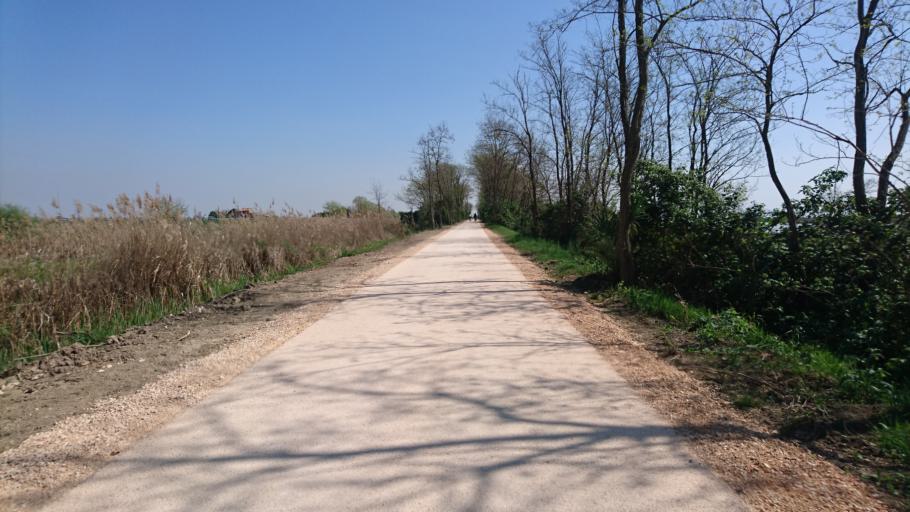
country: IT
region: Veneto
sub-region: Provincia di Venezia
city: Meolo
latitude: 45.5637
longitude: 12.4803
